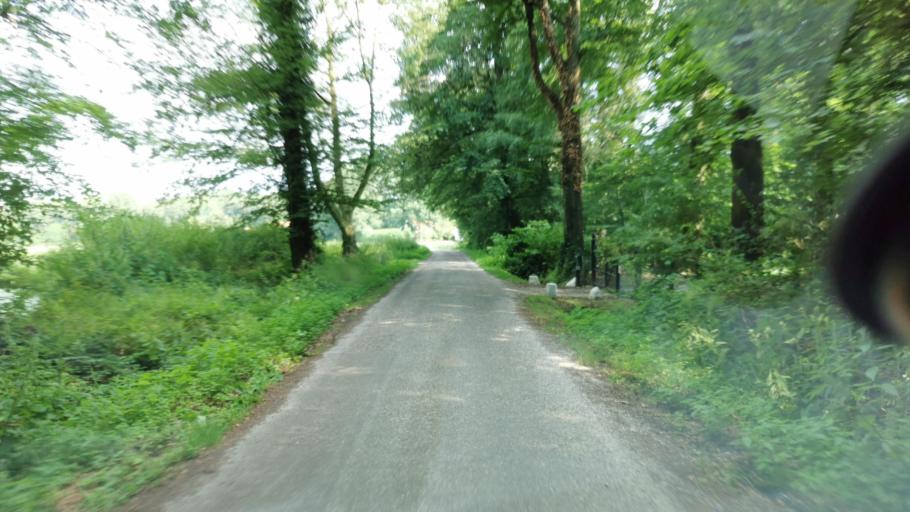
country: NL
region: Overijssel
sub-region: Gemeente Enschede
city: Enschede
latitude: 52.2402
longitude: 6.9352
